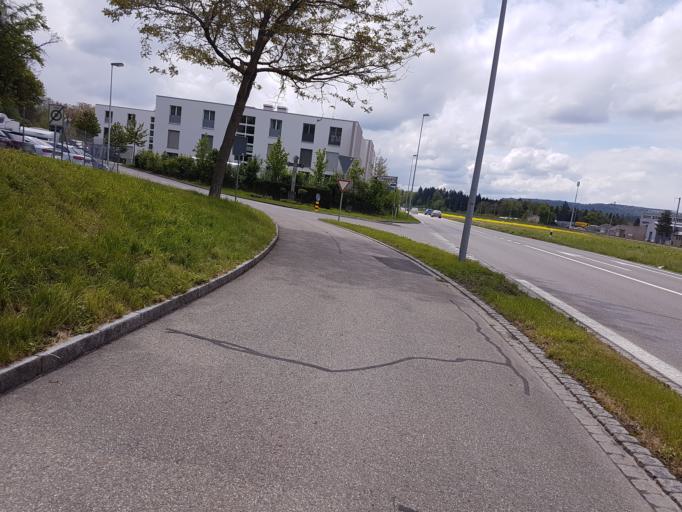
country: CH
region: Aargau
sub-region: Bezirk Zurzach
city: Klingnau
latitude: 47.5609
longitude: 8.2527
